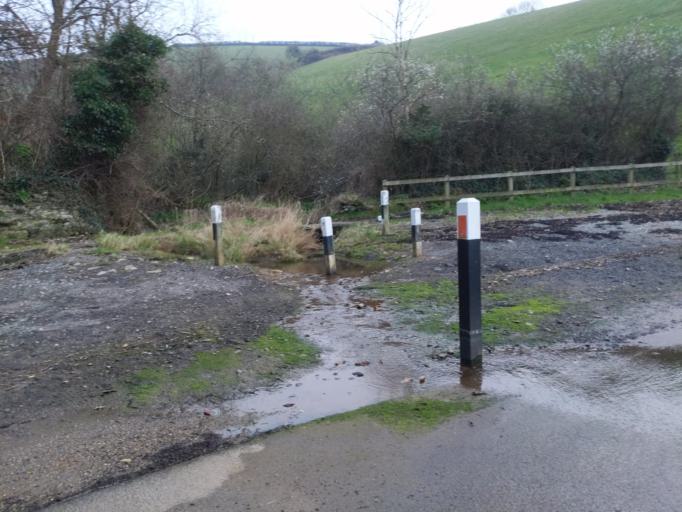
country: GB
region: England
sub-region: Devon
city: Salcombe
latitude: 50.2373
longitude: -3.7452
